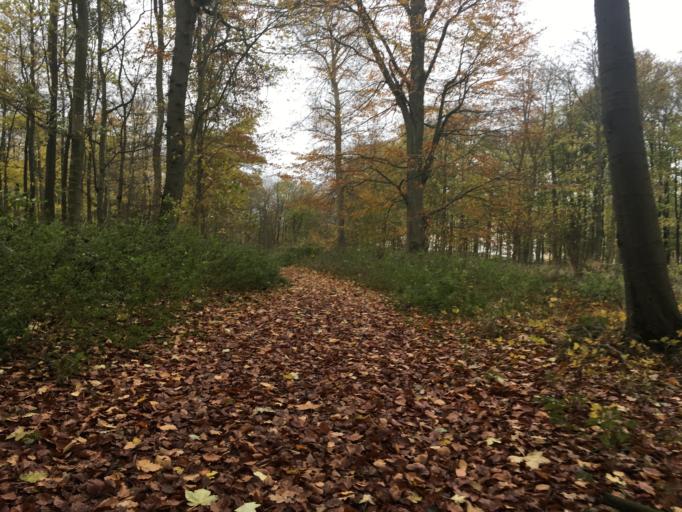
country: DK
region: South Denmark
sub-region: Faaborg-Midtfyn Kommune
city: Faaborg
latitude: 55.0785
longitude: 10.2237
